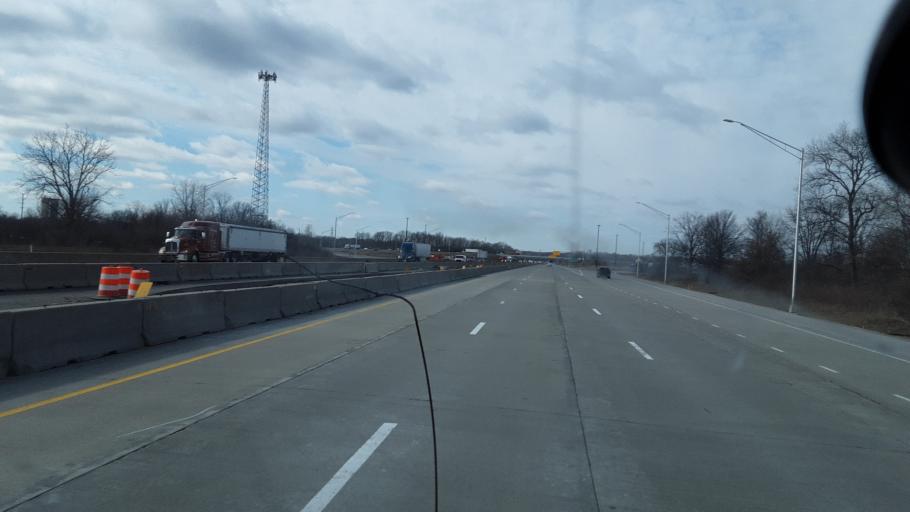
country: US
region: Indiana
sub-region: Hendricks County
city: Plainfield
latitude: 39.6714
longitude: -86.3641
